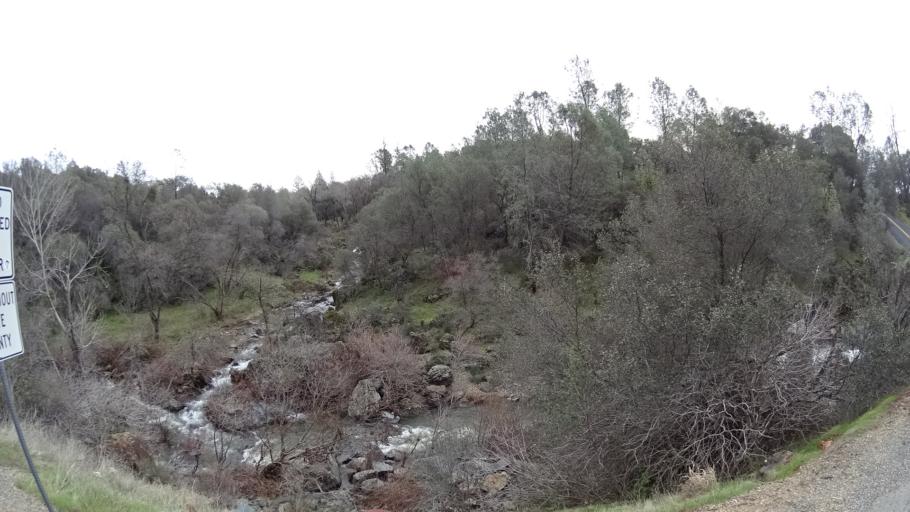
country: US
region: California
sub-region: Yuba County
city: Loma Rica
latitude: 39.3684
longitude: -121.3720
